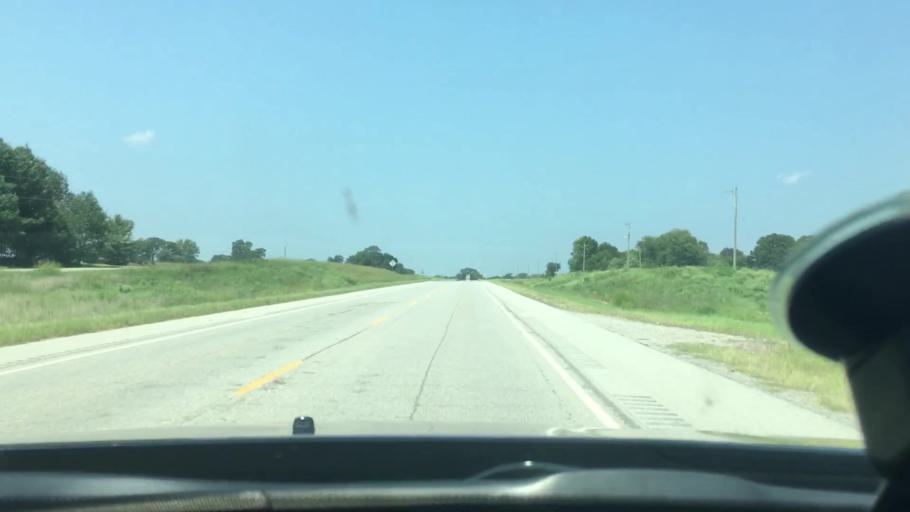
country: US
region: Oklahoma
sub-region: Atoka County
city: Atoka
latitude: 34.2918
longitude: -95.9738
